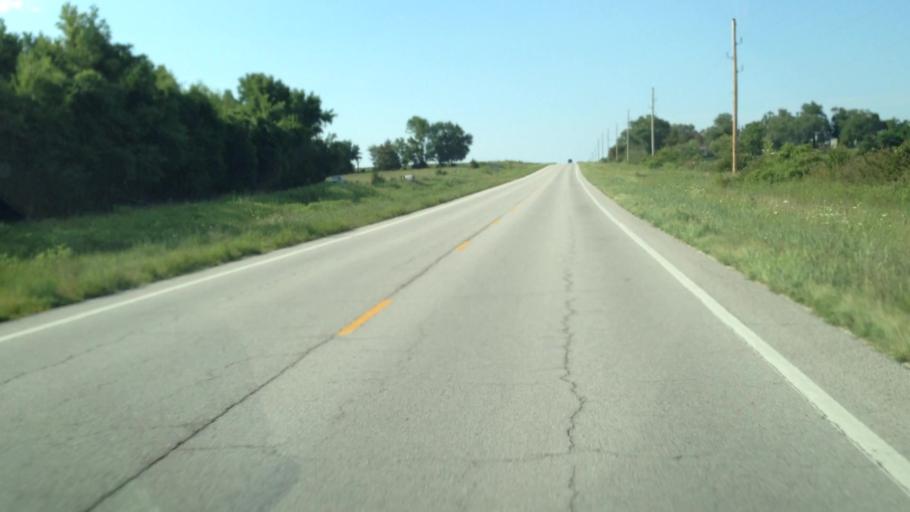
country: US
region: Kansas
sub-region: Allen County
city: Iola
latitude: 37.9955
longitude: -95.1705
